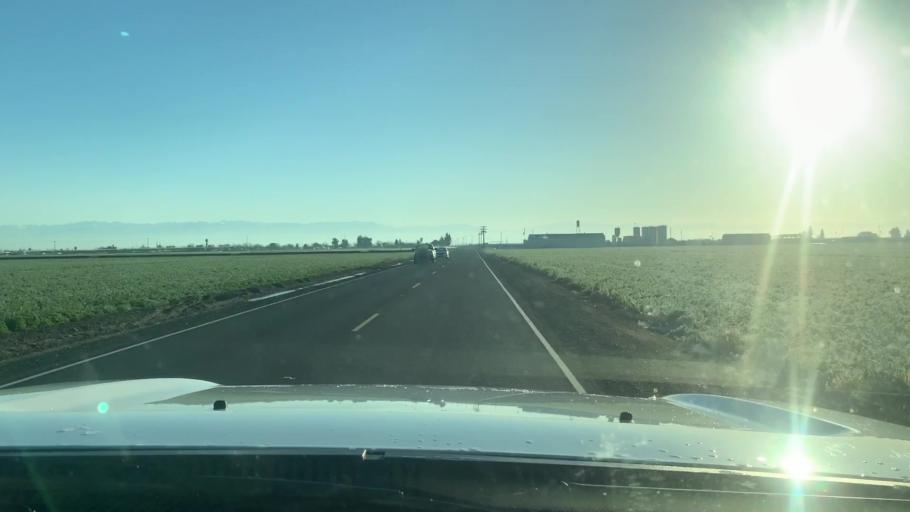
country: US
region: California
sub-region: Kings County
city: Corcoran
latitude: 36.2031
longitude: -119.4822
